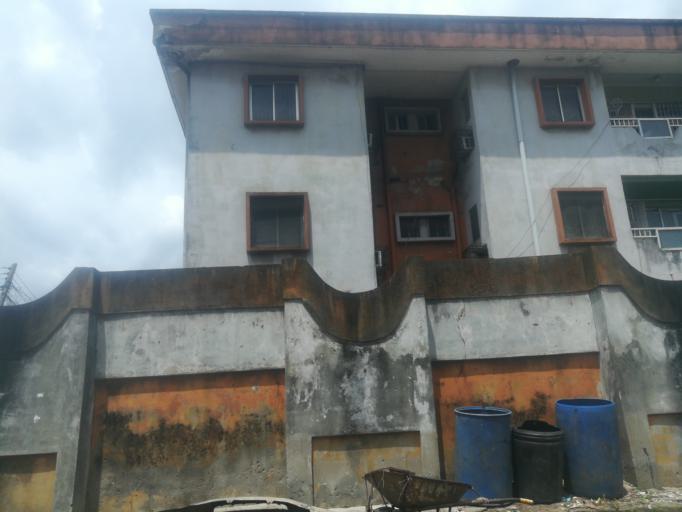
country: NG
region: Lagos
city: Somolu
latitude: 6.5591
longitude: 3.3866
